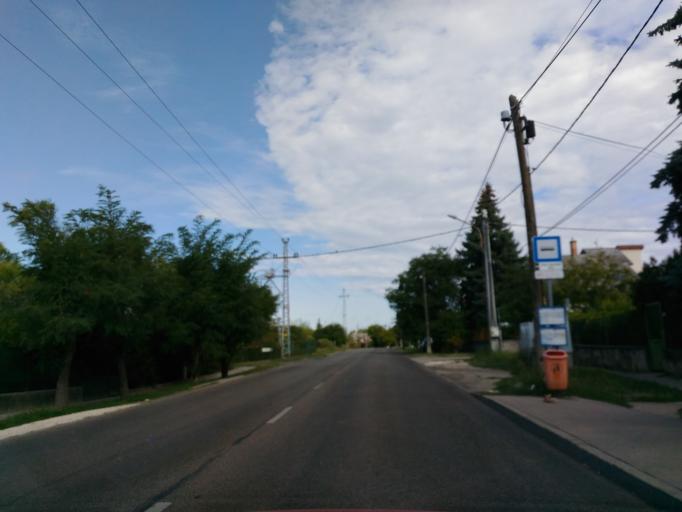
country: HU
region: Pest
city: Diosd
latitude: 47.4092
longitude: 18.9961
